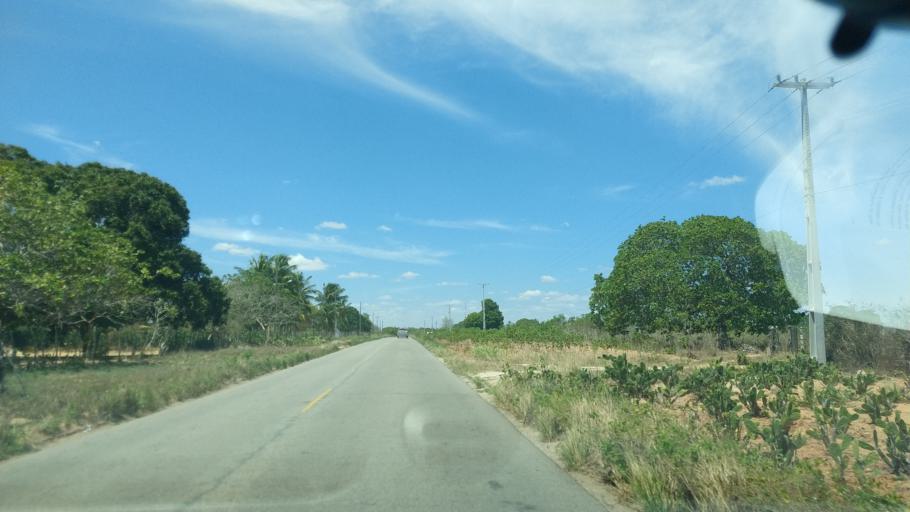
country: BR
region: Rio Grande do Norte
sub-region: Sao Paulo Do Potengi
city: Sao Paulo do Potengi
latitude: -5.9316
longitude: -35.5666
